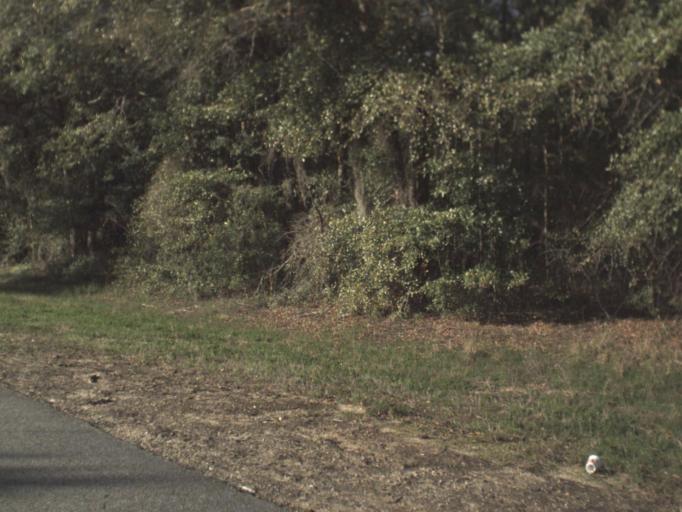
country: US
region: Florida
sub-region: Jackson County
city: Marianna
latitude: 30.6438
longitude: -85.2011
